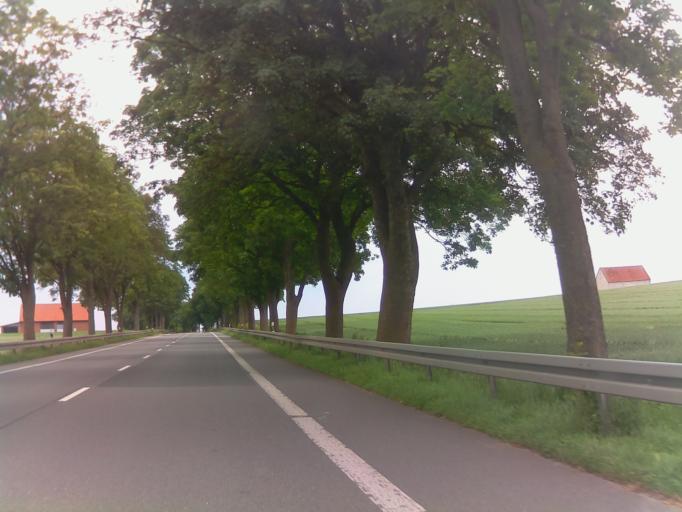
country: DE
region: North Rhine-Westphalia
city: Warburg
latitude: 51.5801
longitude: 9.1314
